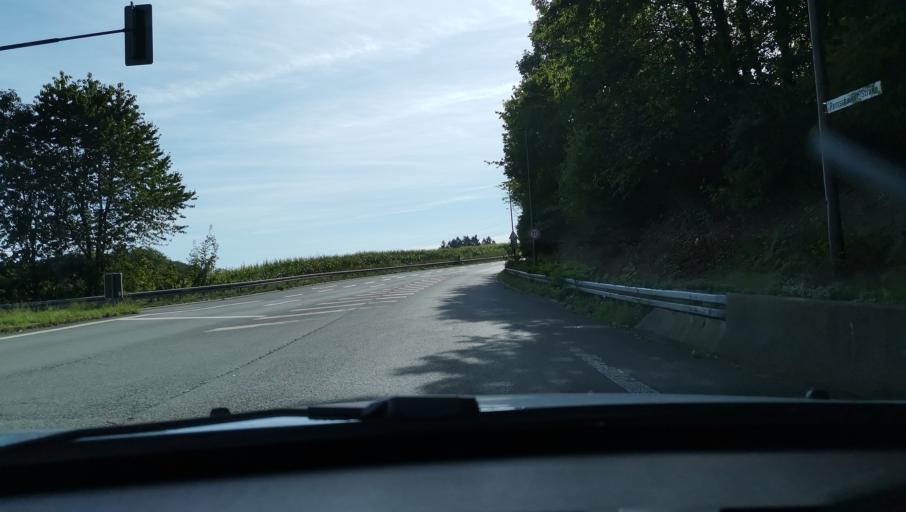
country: DE
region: North Rhine-Westphalia
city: Halver
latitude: 51.1906
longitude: 7.5040
